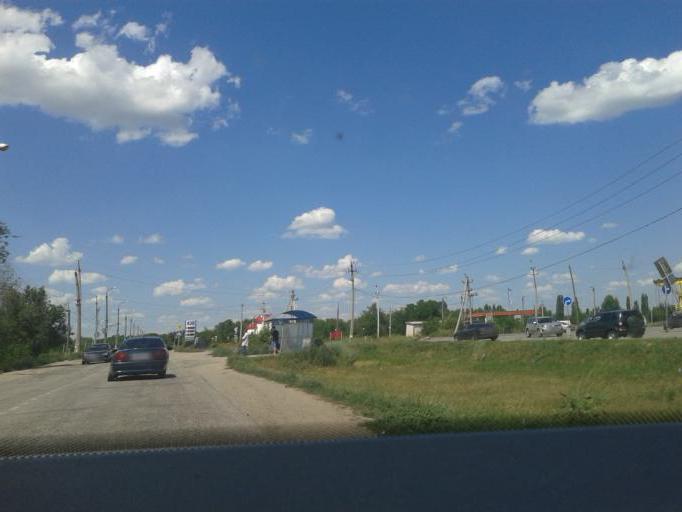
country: RU
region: Volgograd
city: Frolovo
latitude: 49.7514
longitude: 43.6537
